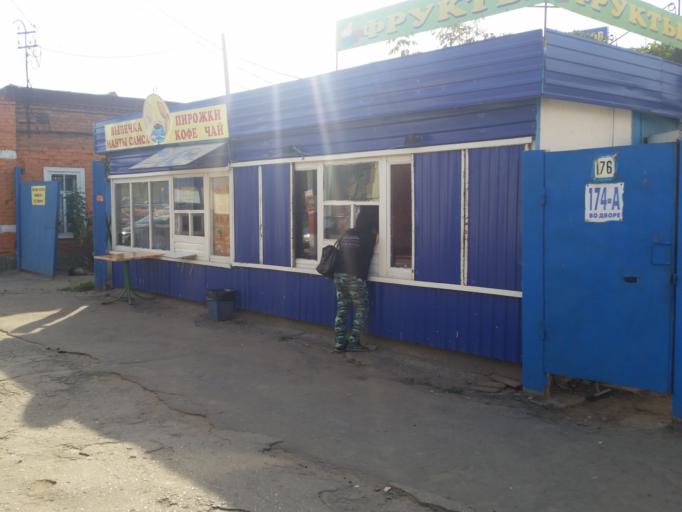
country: RU
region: Ulyanovsk
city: Dimitrovgrad
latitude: 54.2162
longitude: 49.6211
